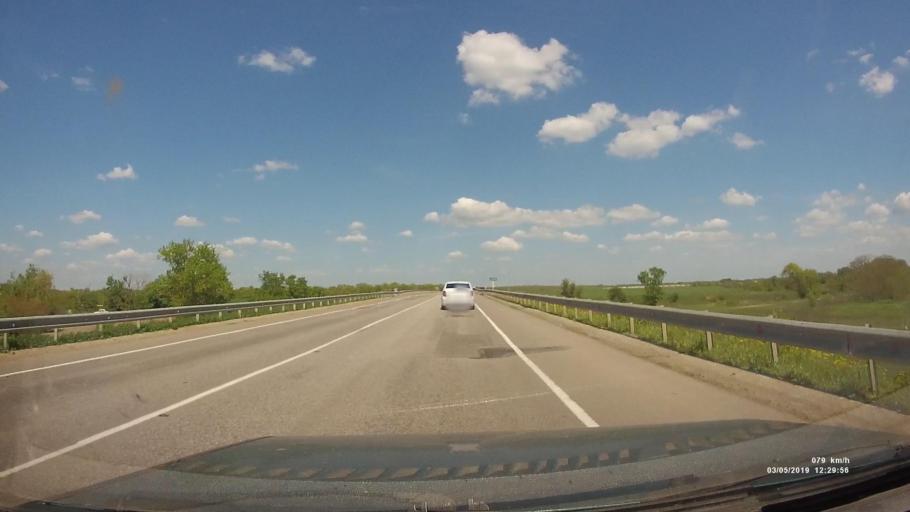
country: RU
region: Rostov
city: Semikarakorsk
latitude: 47.4942
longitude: 40.7394
